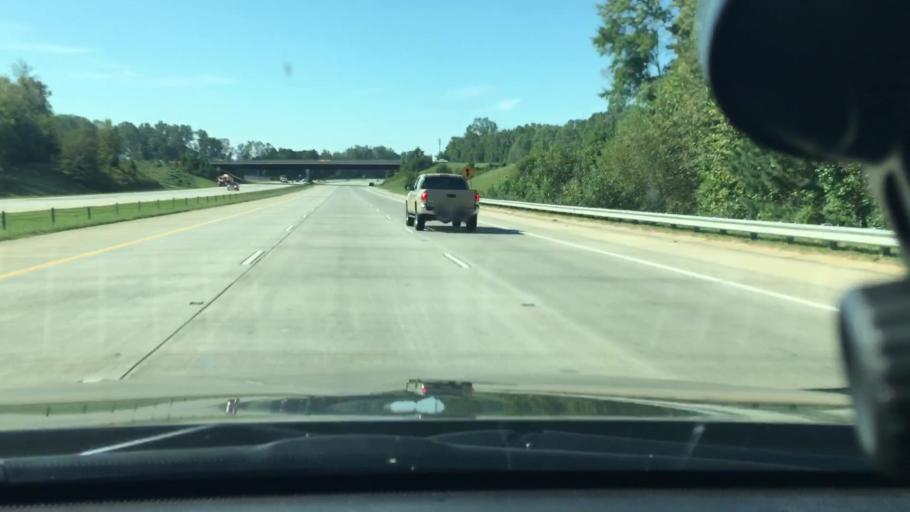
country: US
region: North Carolina
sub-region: Mecklenburg County
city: Huntersville
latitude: 35.3534
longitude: -80.8631
